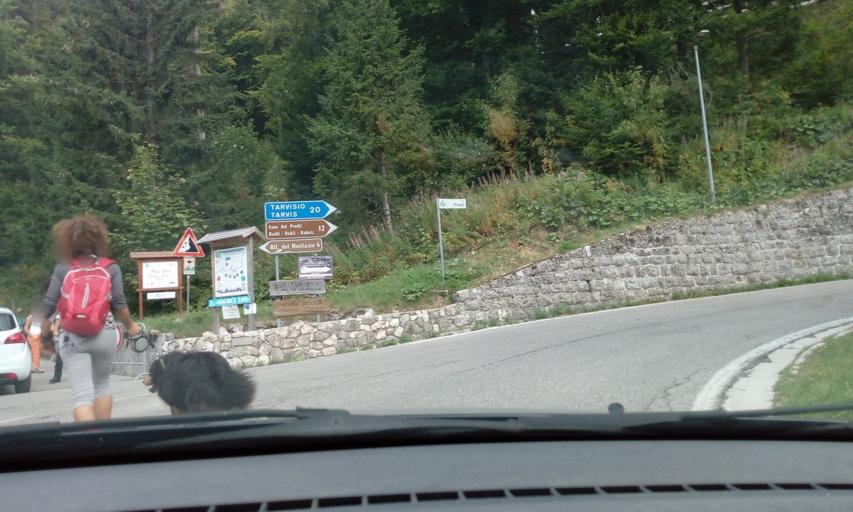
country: SI
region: Bovec
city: Bovec
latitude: 46.3913
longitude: 13.4722
